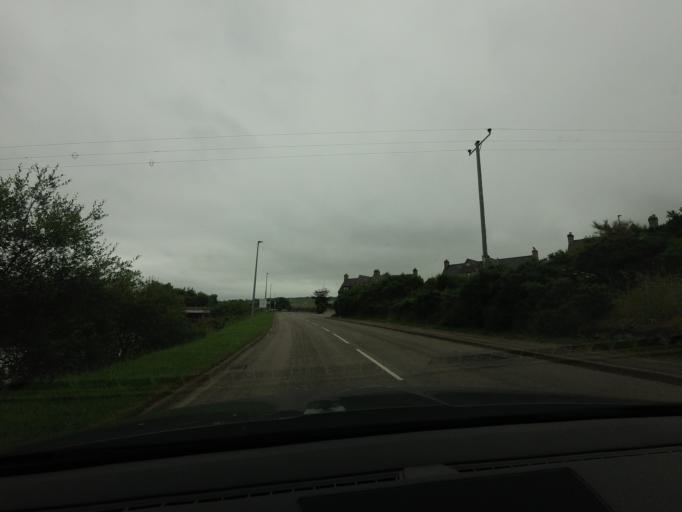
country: GB
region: Scotland
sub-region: Highland
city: Alness
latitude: 58.0197
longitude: -4.4036
